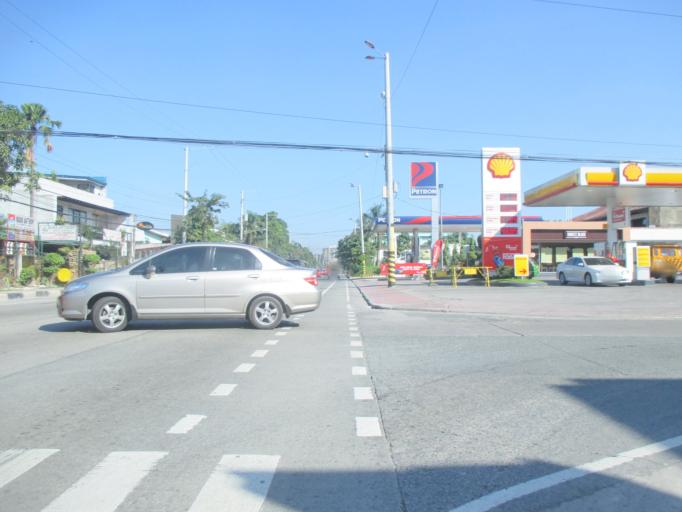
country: PH
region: Metro Manila
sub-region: Marikina
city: Calumpang
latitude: 14.6272
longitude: 121.1022
